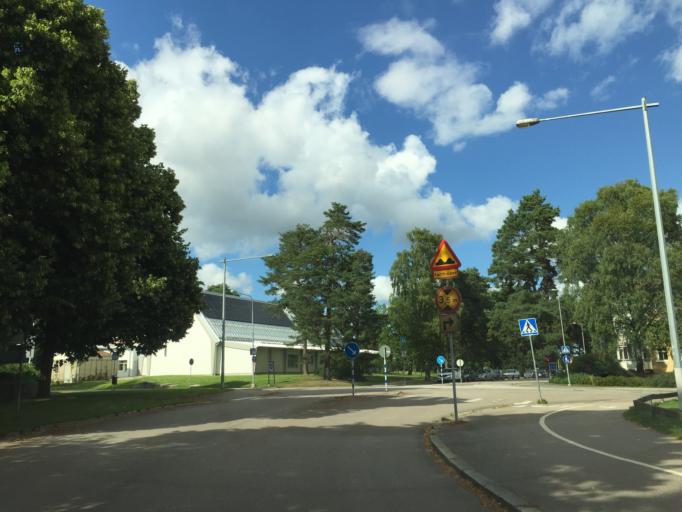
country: SE
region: Vaestra Goetaland
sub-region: Trollhattan
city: Trollhattan
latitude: 58.2867
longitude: 12.3047
